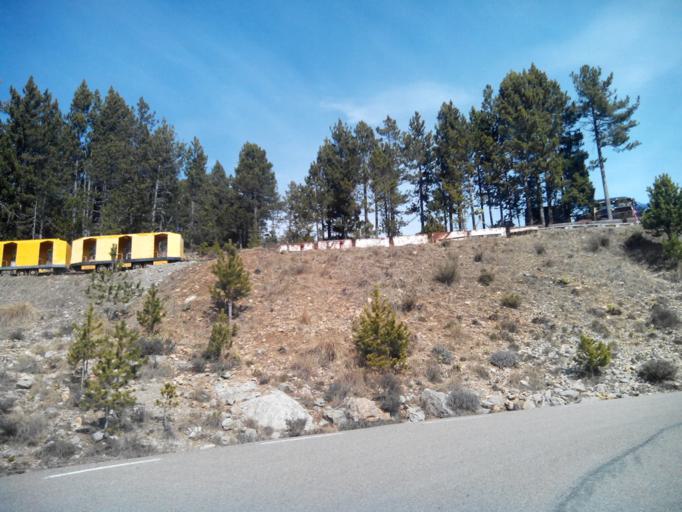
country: ES
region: Catalonia
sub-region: Provincia de Barcelona
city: Vallcebre
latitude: 42.2009
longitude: 1.7835
